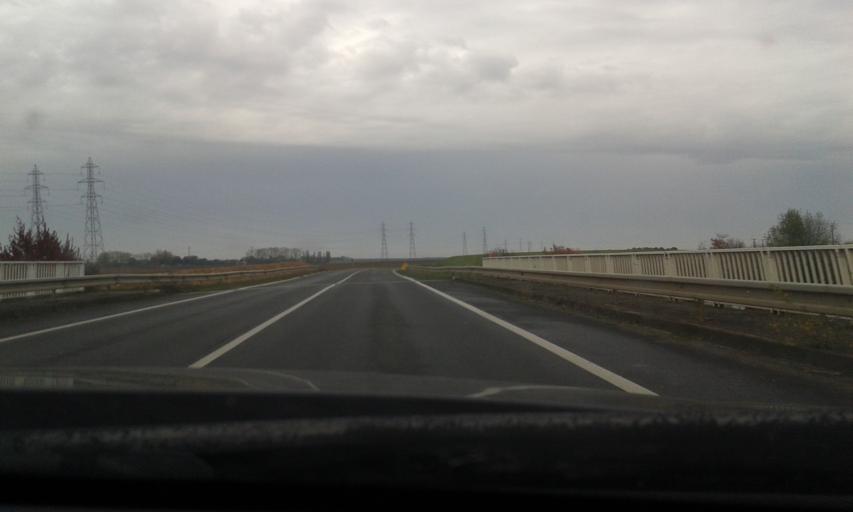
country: FR
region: Centre
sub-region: Departement d'Eure-et-Loir
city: Baigneaux
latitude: 48.1294
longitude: 1.8533
